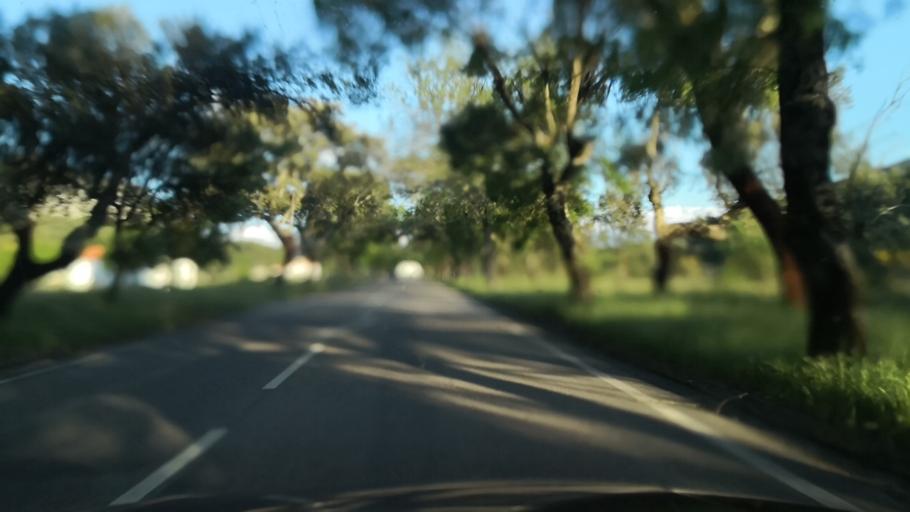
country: PT
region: Portalegre
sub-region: Portalegre
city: Sao Juliao
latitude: 39.3551
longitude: -7.3121
